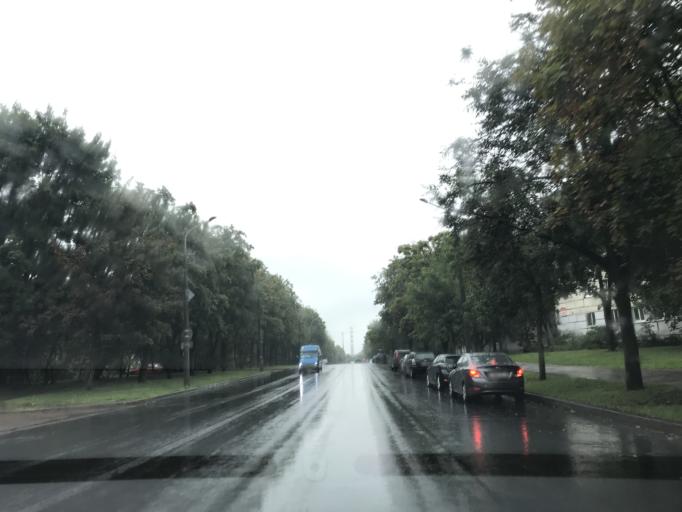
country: BY
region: Minsk
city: Minsk
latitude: 53.9379
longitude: 27.6088
